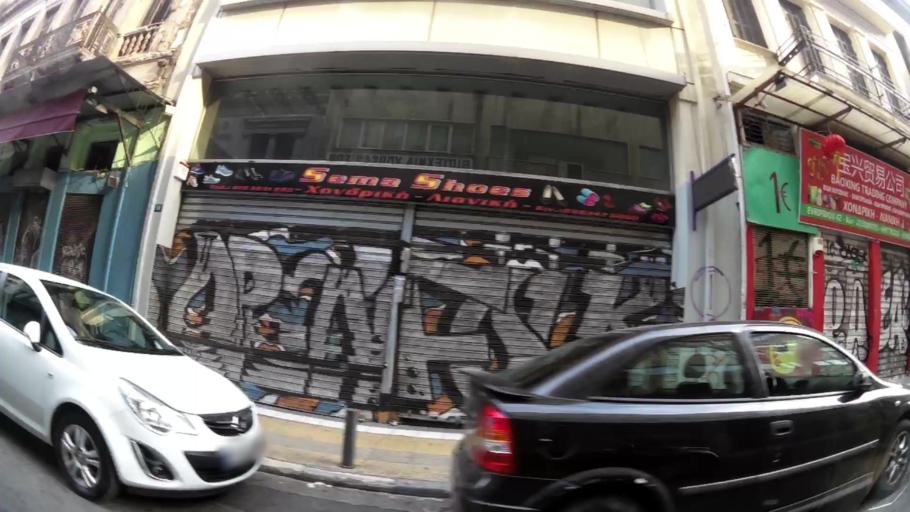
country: GR
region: Attica
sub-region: Nomarchia Athinas
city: Athens
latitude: 37.9802
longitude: 23.7249
